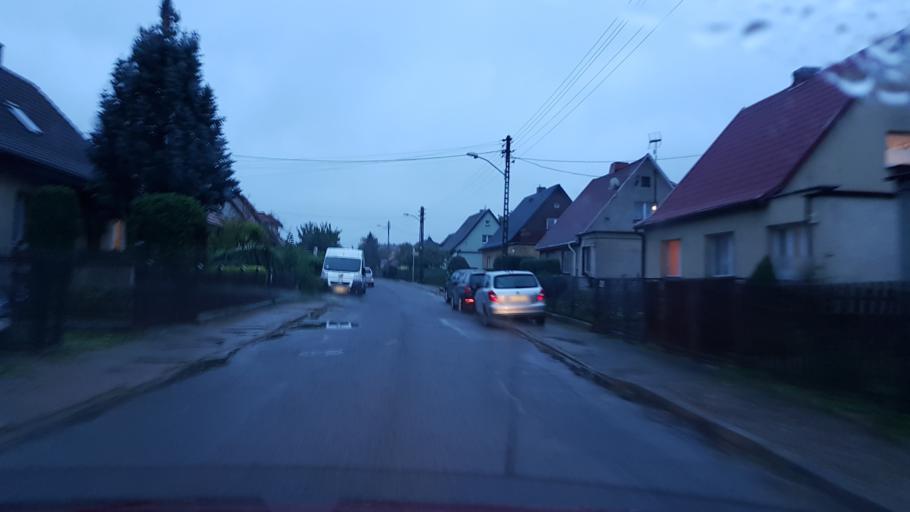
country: PL
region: West Pomeranian Voivodeship
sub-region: Powiat policki
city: Przeclaw
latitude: 53.4051
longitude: 14.5082
